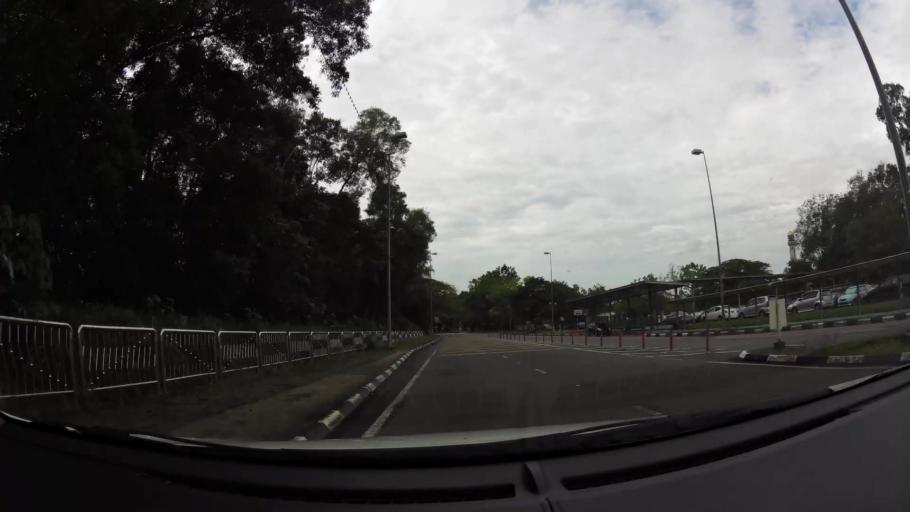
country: BN
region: Brunei and Muara
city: Bandar Seri Begawan
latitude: 4.8998
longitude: 114.9243
